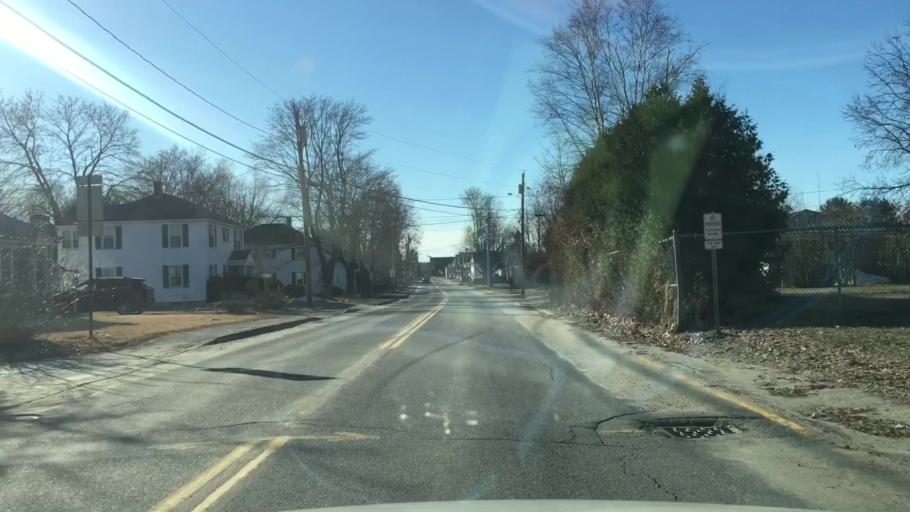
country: US
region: Maine
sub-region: Kennebec County
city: Winslow
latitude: 44.5498
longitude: -69.6210
